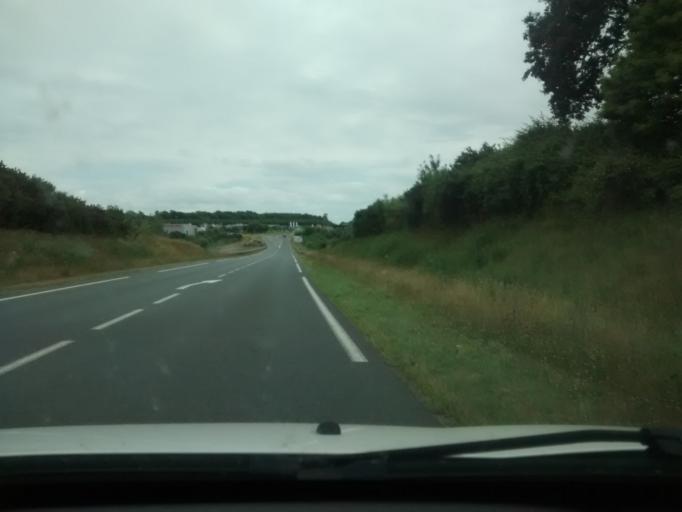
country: FR
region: Brittany
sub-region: Departement des Cotes-d'Armor
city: Lannion
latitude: 48.7392
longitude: -3.4397
